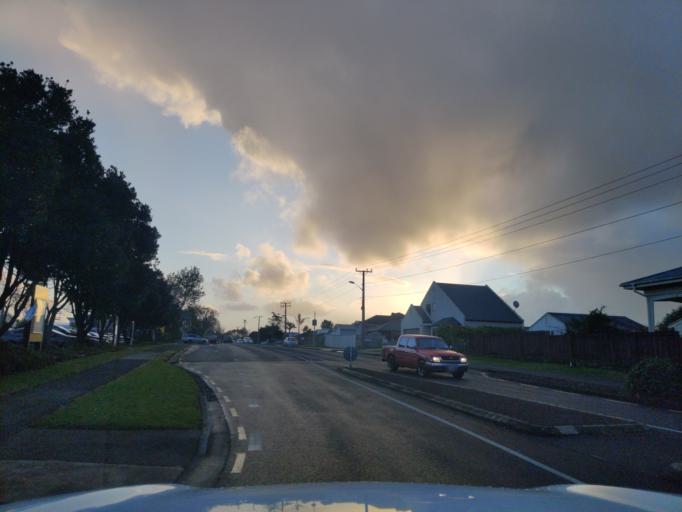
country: NZ
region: Auckland
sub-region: Auckland
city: Pukekohe East
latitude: -37.2044
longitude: 174.9007
